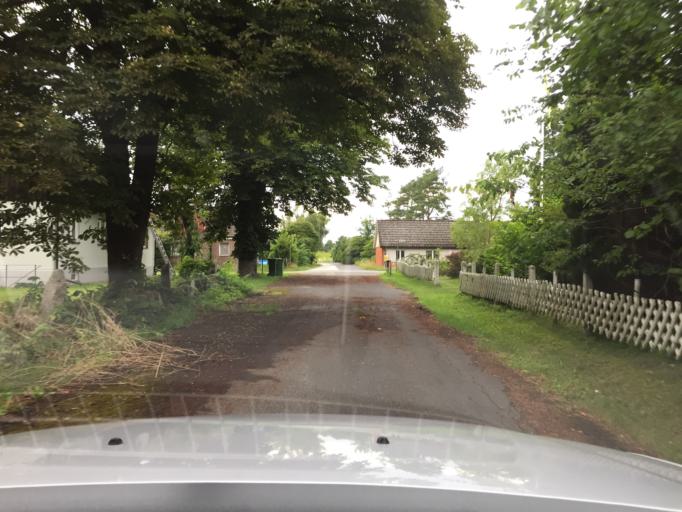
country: SE
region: Skane
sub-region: Kristianstads Kommun
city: Norra Asum
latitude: 55.9350
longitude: 14.0757
